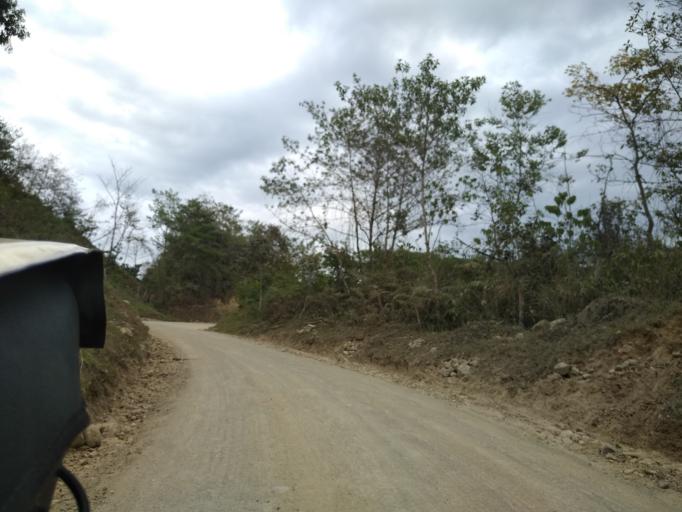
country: PE
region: Cajamarca
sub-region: Provincia de San Ignacio
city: Namballe
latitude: -4.9348
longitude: -79.1036
